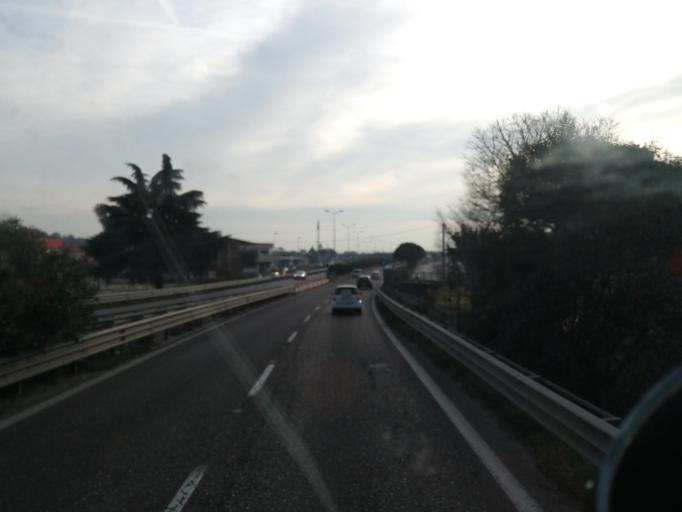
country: IT
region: Lombardy
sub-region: Provincia di Brescia
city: Desenzano del Garda
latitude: 45.4488
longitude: 10.5207
